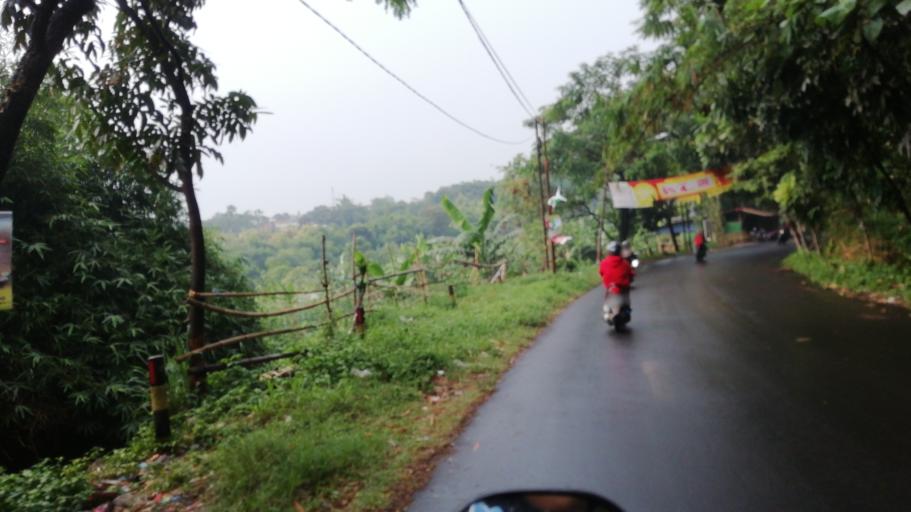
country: ID
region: West Java
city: Bogor
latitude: -6.5330
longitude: 106.8061
